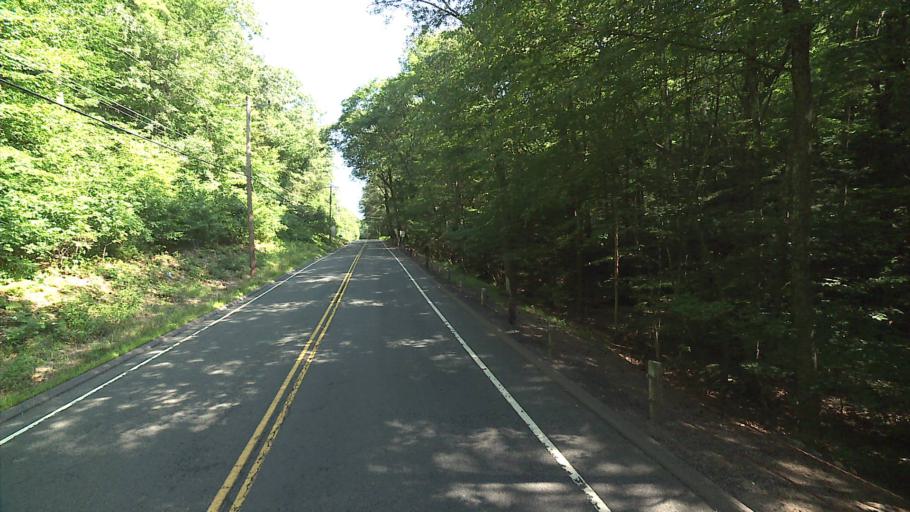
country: US
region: Connecticut
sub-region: Hartford County
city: North Granby
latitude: 41.9765
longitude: -72.8888
